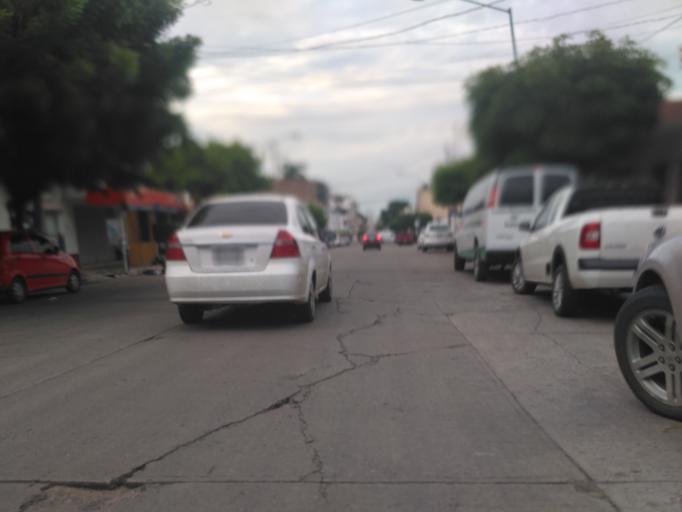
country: MX
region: Sinaloa
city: Culiacan
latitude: 24.8002
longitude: -107.3975
